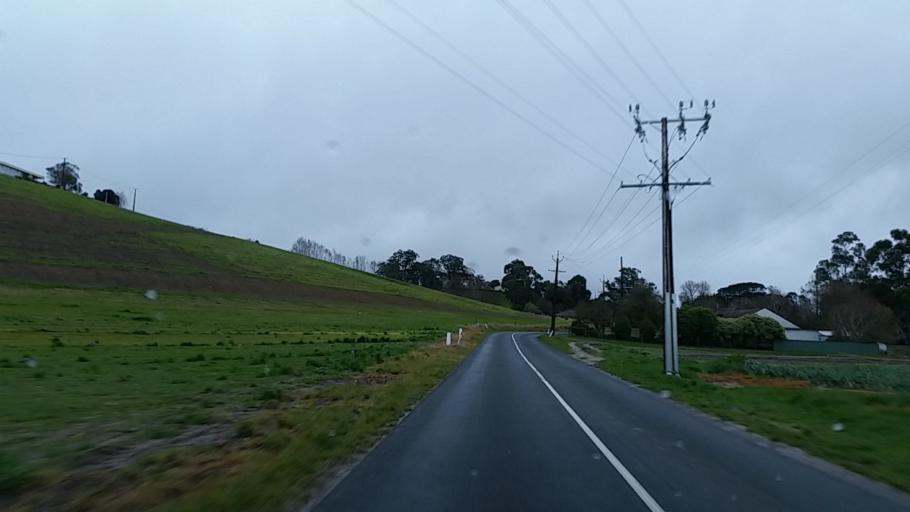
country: AU
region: South Australia
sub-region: Adelaide Hills
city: Bridgewater
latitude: -34.9614
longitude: 138.7410
